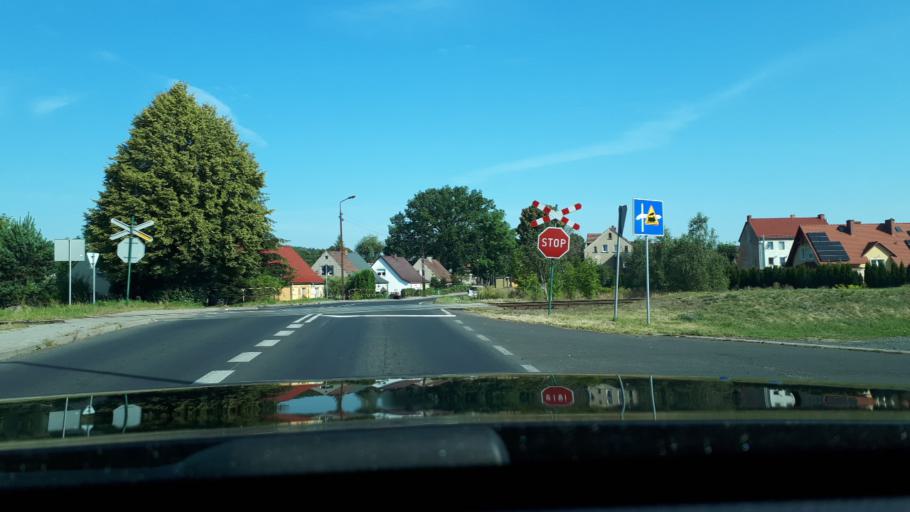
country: PL
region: Lower Silesian Voivodeship
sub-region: Powiat lubanski
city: Luban
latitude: 51.0994
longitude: 15.2943
